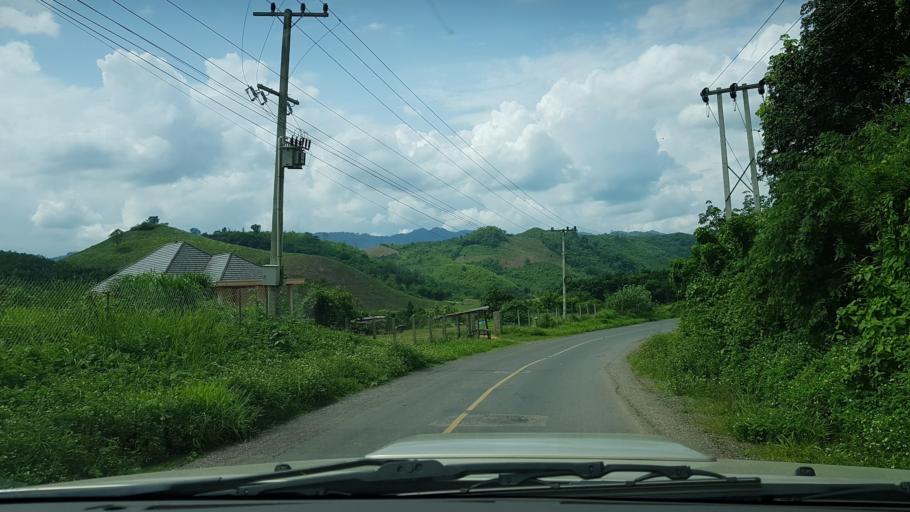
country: LA
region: Loungnamtha
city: Muang Nale
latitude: 20.1612
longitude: 101.5049
